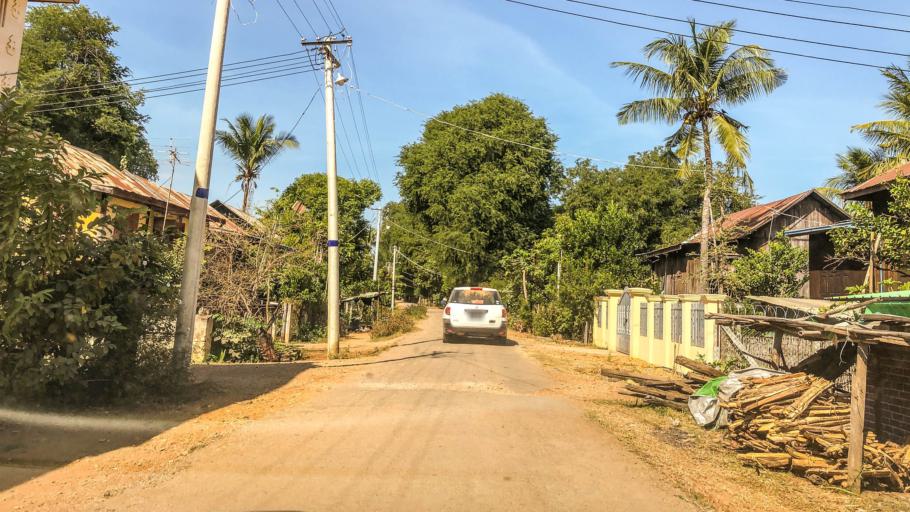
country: MM
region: Magway
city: Magway
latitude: 19.9739
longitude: 95.0391
